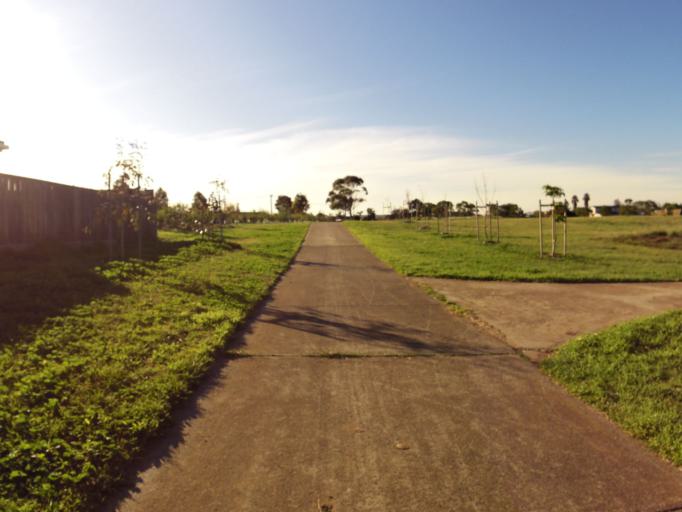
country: AU
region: Victoria
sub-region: Wyndham
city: Hoppers Crossing
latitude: -37.8665
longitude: 144.7146
